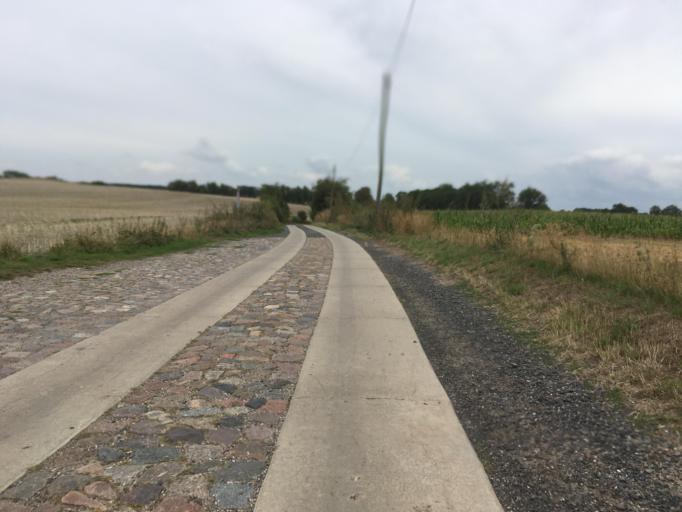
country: DE
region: Brandenburg
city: Gerswalde
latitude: 53.2025
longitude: 13.8312
